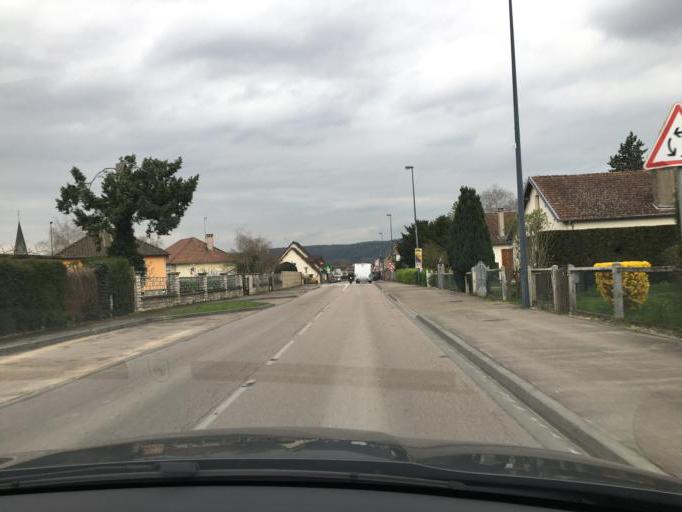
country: FR
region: Haute-Normandie
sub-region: Departement de l'Eure
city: Courcelles-sur-Seine
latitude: 49.1838
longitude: 1.3604
